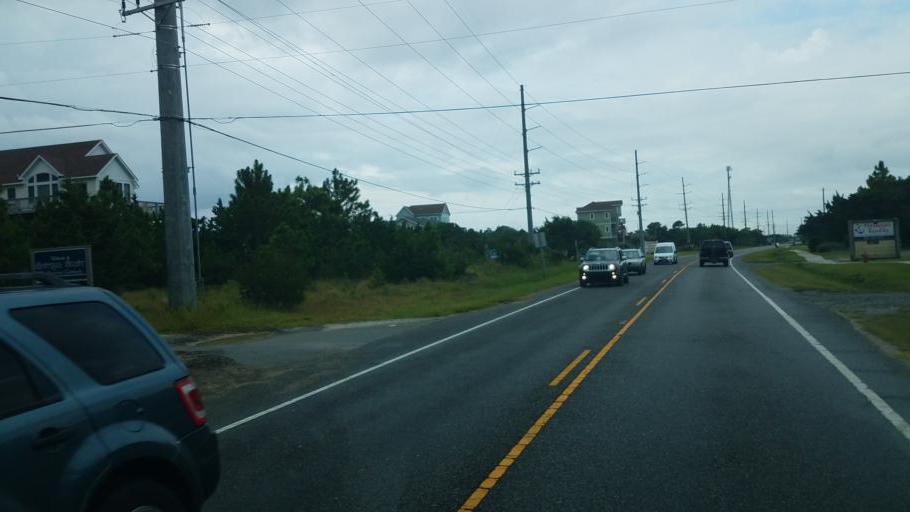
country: US
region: North Carolina
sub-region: Dare County
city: Buxton
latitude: 35.5706
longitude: -75.4676
